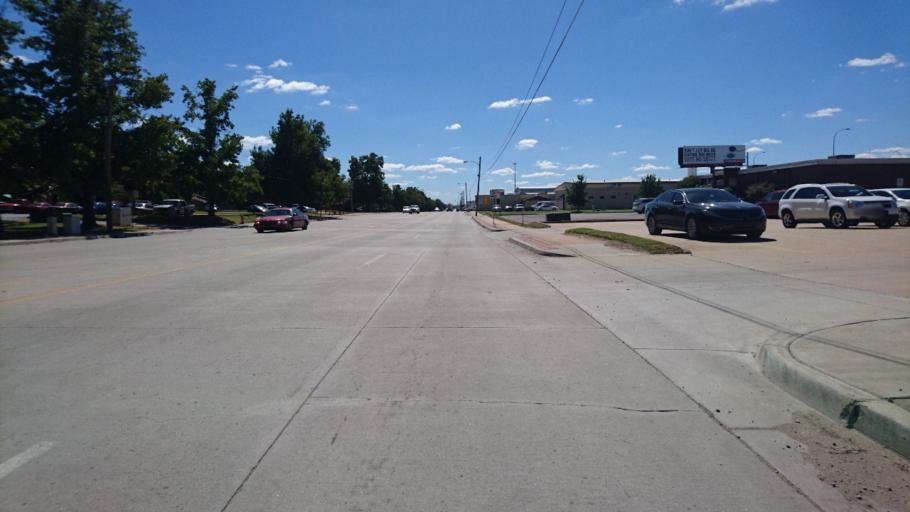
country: US
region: Oklahoma
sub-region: Tulsa County
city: Tulsa
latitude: 36.1371
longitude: -96.0071
